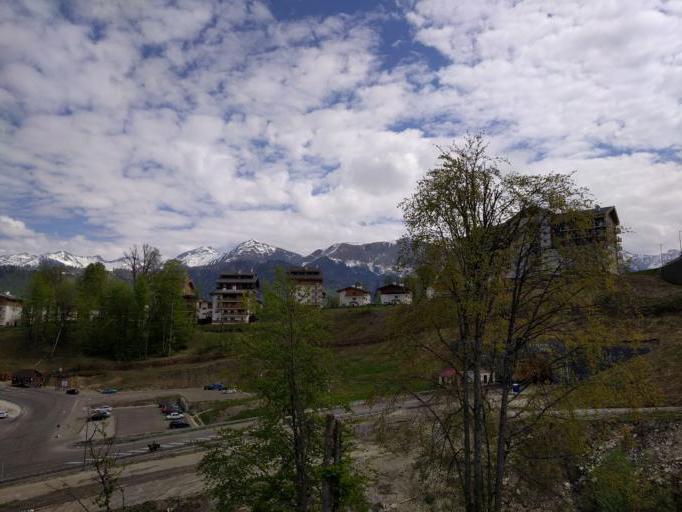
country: RU
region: Krasnodarskiy
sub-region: Sochi City
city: Krasnaya Polyana
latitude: 43.6608
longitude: 40.3154
